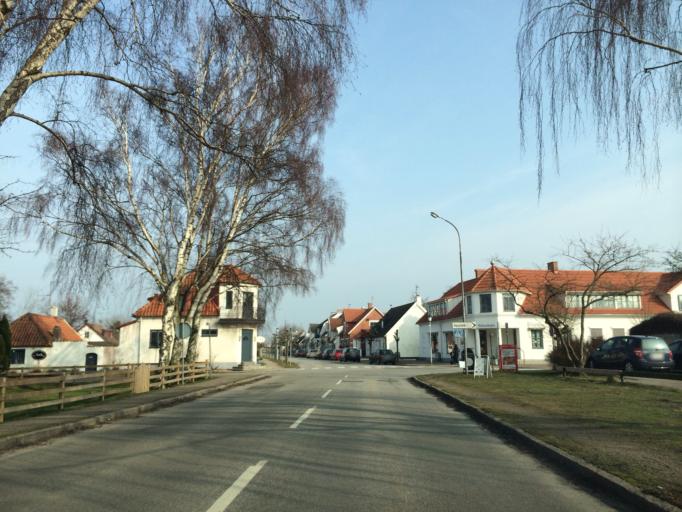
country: SE
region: Skane
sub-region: Vellinge Kommun
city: Skanor med Falsterbo
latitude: 55.4123
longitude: 12.8431
